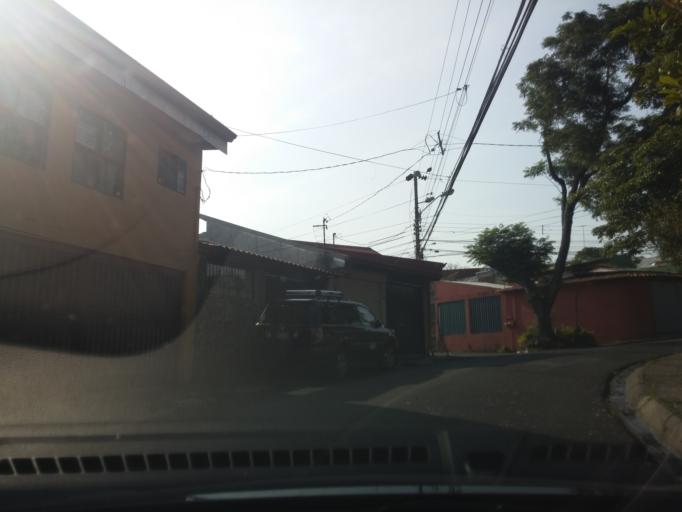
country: CR
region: Heredia
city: Llorente
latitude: 9.9928
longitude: -84.1451
